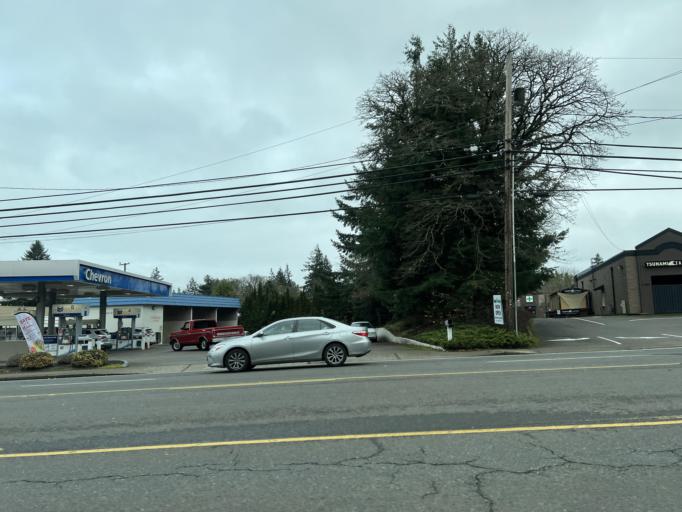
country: US
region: Oregon
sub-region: Marion County
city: Salem
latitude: 44.8922
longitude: -123.0355
